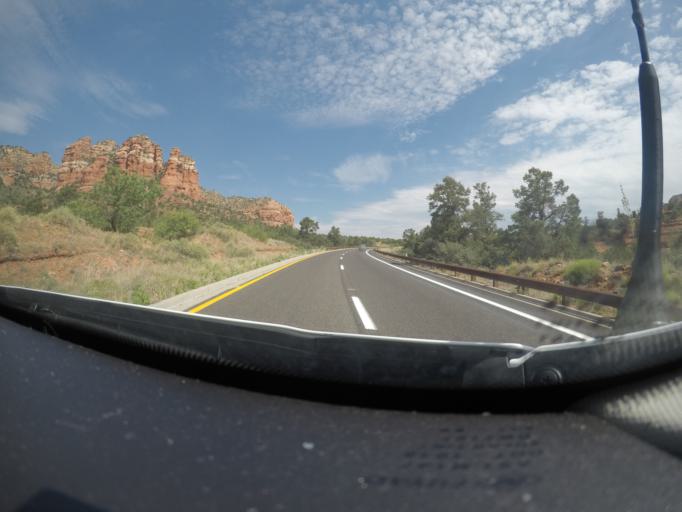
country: US
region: Arizona
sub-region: Yavapai County
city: Village of Oak Creek (Big Park)
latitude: 34.7988
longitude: -111.7668
